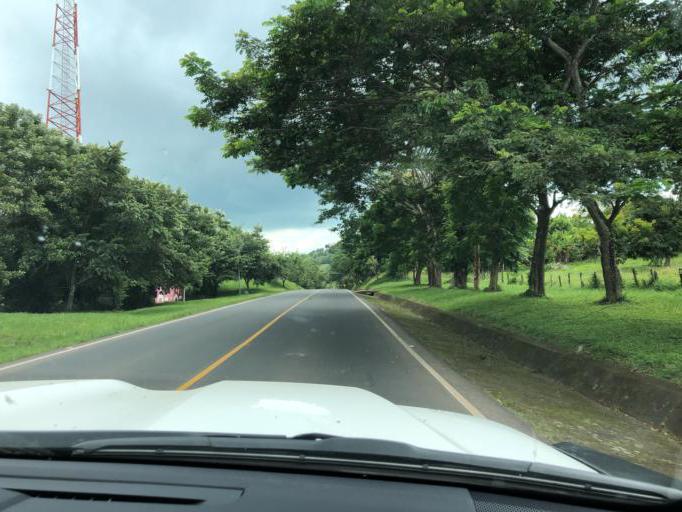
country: NI
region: Chontales
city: Villa Sandino
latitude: 12.0547
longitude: -85.0350
